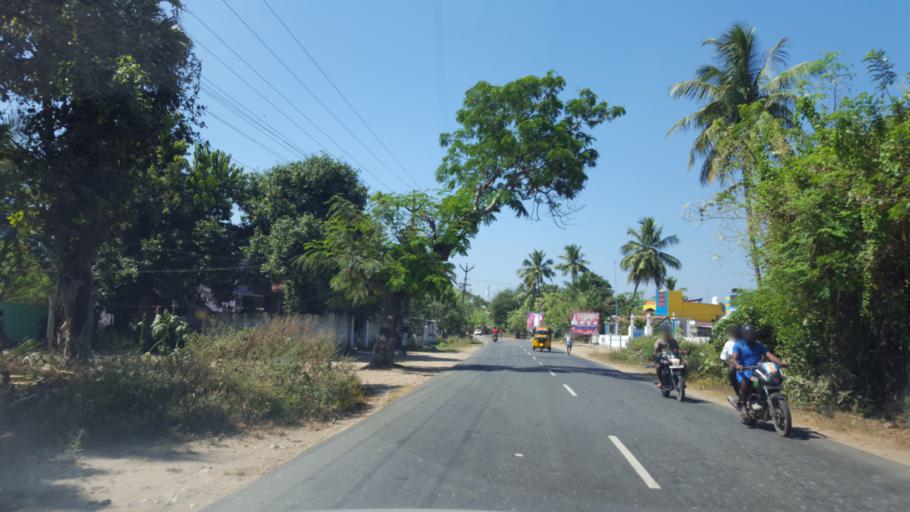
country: IN
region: Tamil Nadu
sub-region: Kancheepuram
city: Chengalpattu
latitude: 12.7272
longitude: 79.9502
